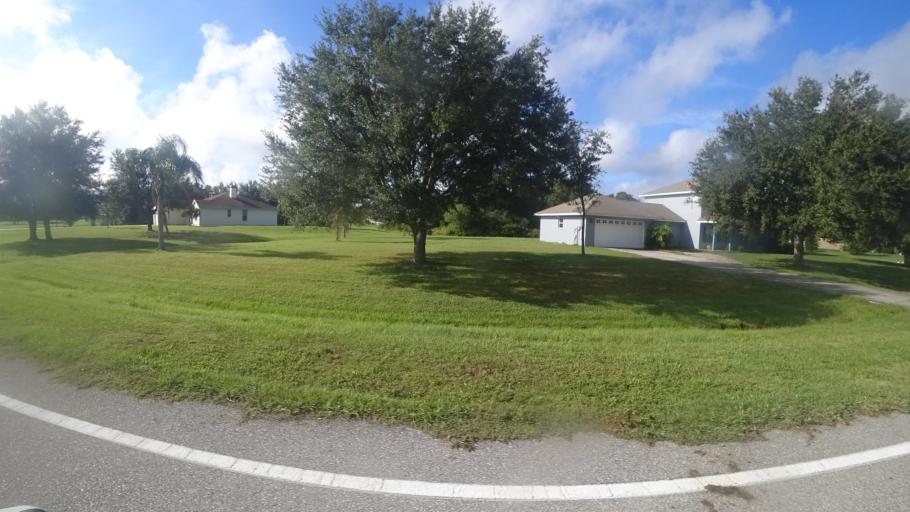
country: US
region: Florida
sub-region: Hillsborough County
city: Sun City Center
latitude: 27.5556
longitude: -82.3598
